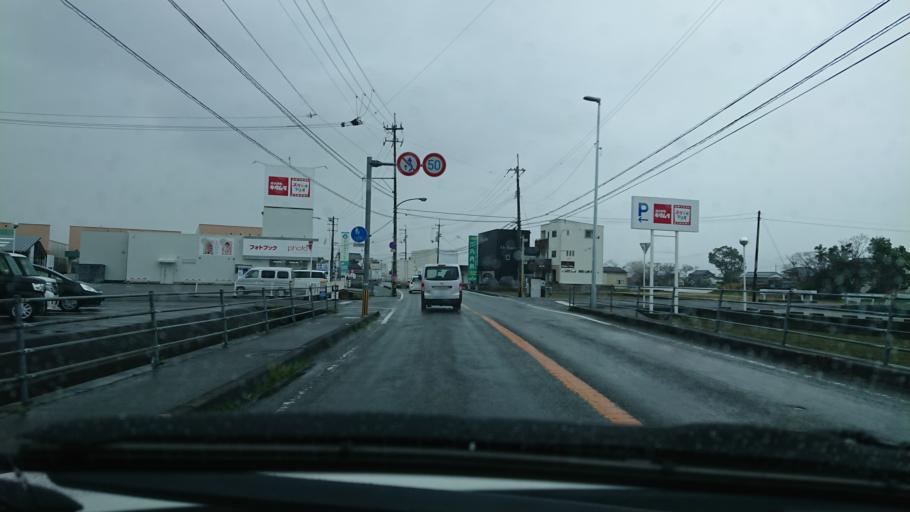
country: JP
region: Tokushima
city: Ishii
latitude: 34.0867
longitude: 134.4903
